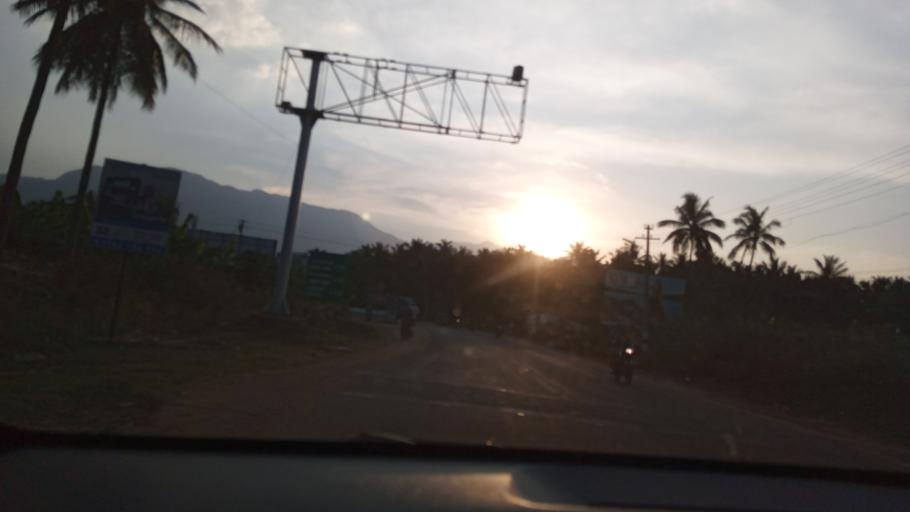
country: IN
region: Tamil Nadu
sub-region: Coimbatore
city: Perur
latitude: 10.9458
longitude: 76.7723
